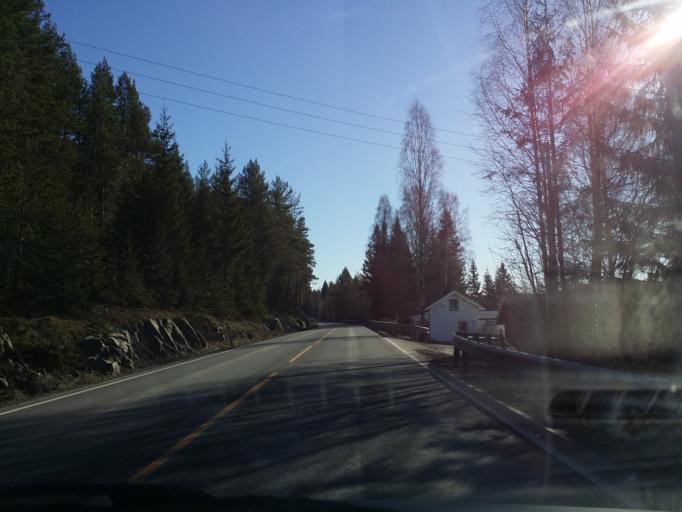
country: NO
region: Buskerud
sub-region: Ringerike
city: Honefoss
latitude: 60.2603
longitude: 10.1887
